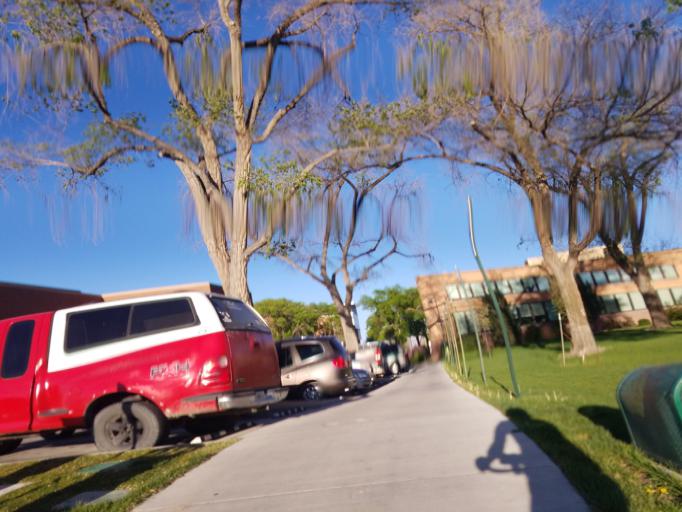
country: US
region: Colorado
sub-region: Mesa County
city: Grand Junction
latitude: 39.0782
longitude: -108.5546
